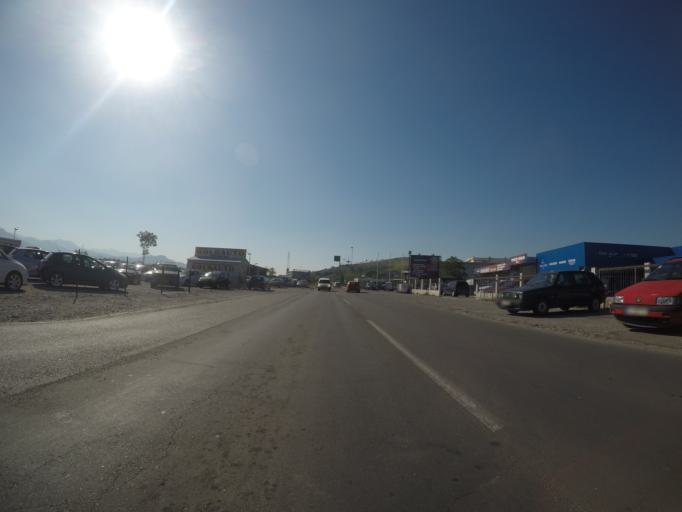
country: ME
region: Podgorica
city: Podgorica
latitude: 42.4298
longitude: 19.2318
